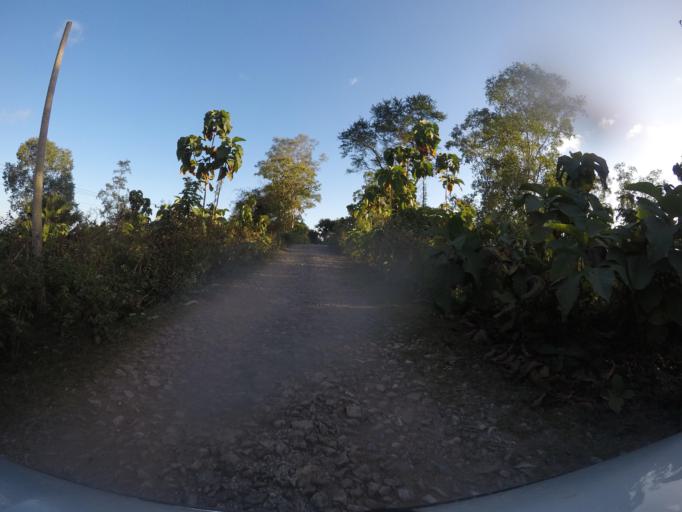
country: TL
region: Baucau
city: Venilale
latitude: -8.7184
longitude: 126.7122
